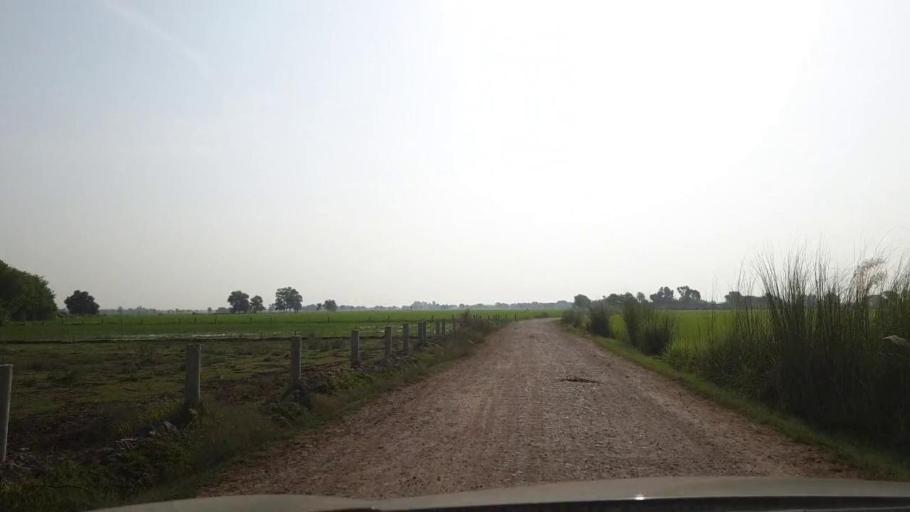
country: PK
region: Sindh
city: Larkana
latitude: 27.4921
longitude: 68.2065
